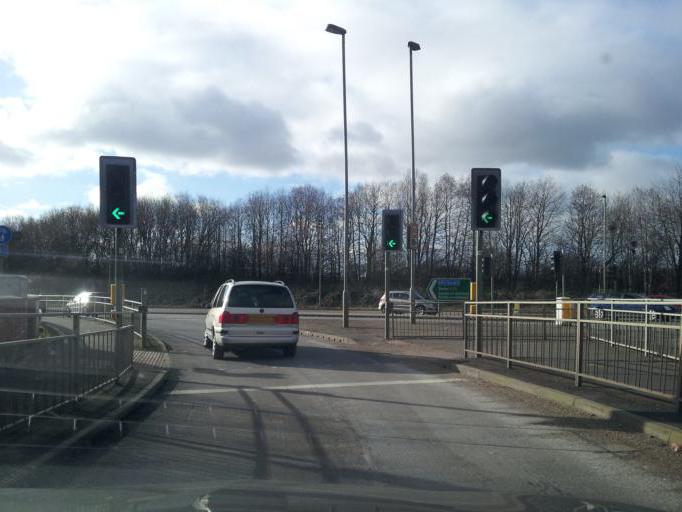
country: GB
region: England
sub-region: Nottinghamshire
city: Sutton in Ashfield
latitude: 53.1279
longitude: -1.2355
